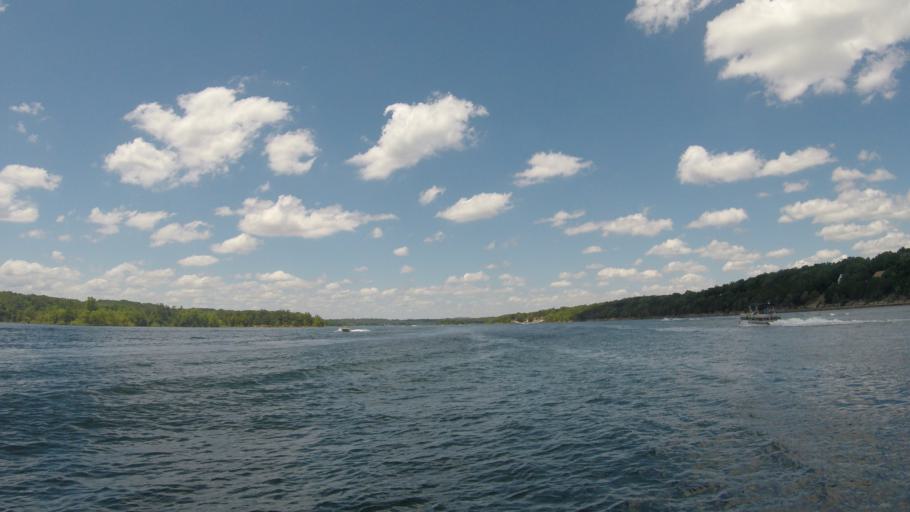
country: US
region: Missouri
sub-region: Barry County
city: Shell Knob
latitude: 36.5900
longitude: -93.5419
